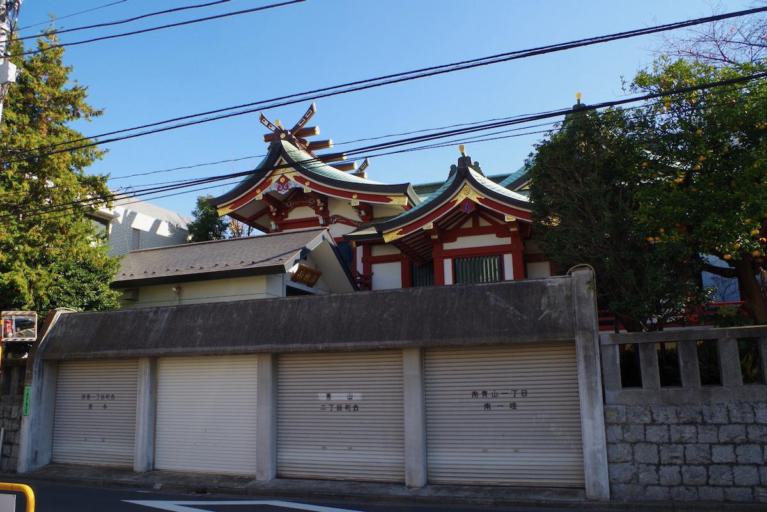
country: JP
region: Tokyo
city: Tokyo
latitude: 35.6725
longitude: 139.7138
